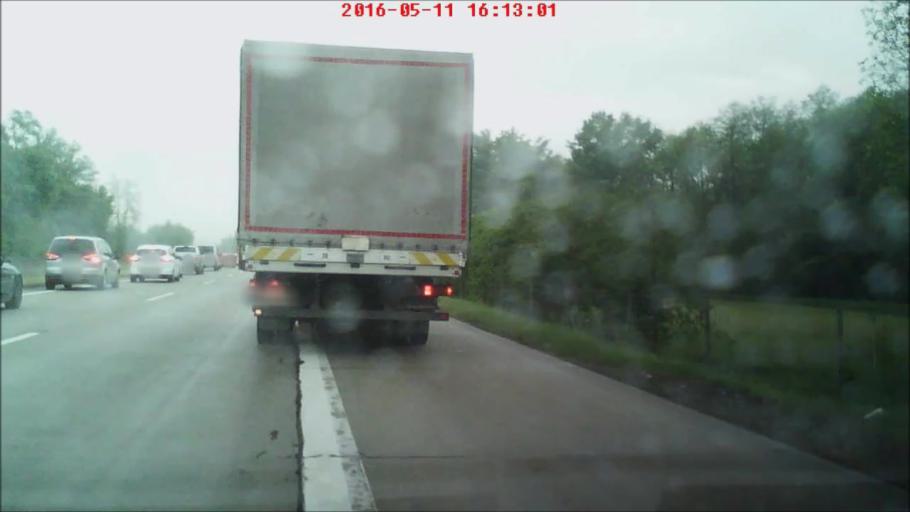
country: AT
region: Styria
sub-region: Politischer Bezirk Leibnitz
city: Gabersdorf
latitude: 46.7846
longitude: 15.5755
